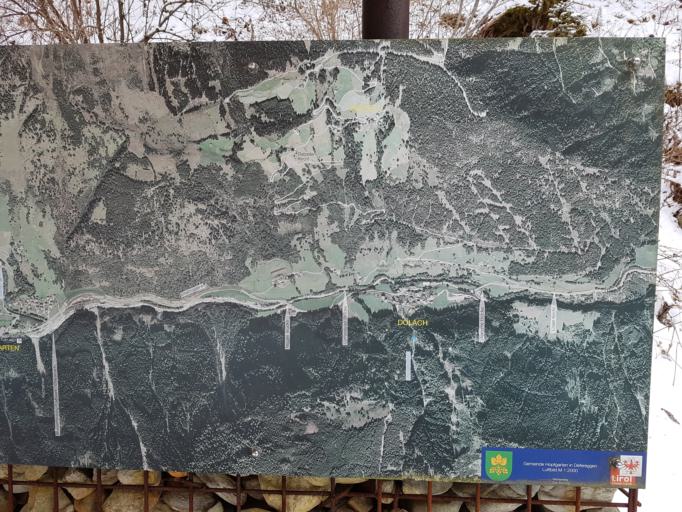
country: AT
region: Tyrol
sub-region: Politischer Bezirk Lienz
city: Hopfgarten in Defereggen
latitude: 46.9184
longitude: 12.5010
